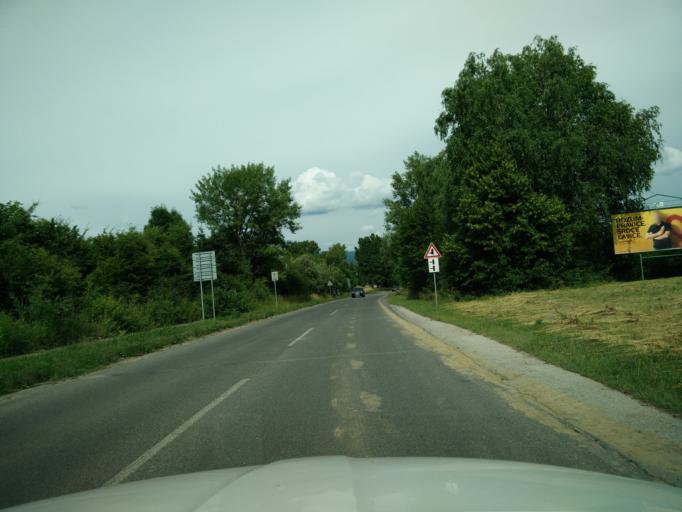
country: SK
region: Nitriansky
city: Bojnice
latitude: 48.7734
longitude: 18.5801
